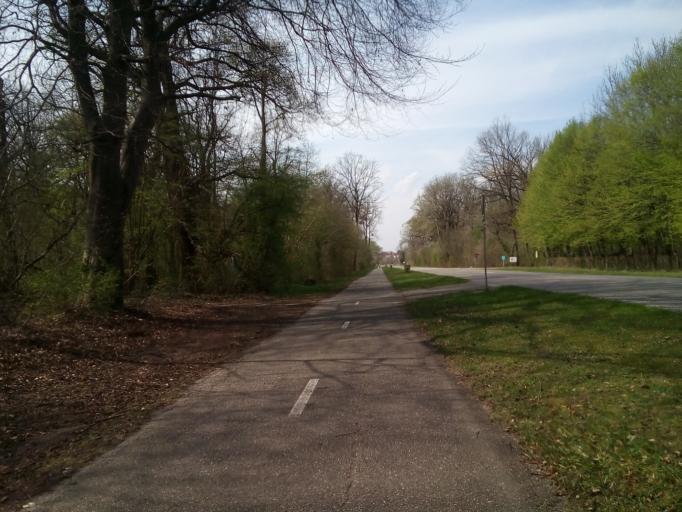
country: FR
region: Alsace
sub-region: Departement du Bas-Rhin
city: Seltz
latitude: 48.8902
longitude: 8.1207
